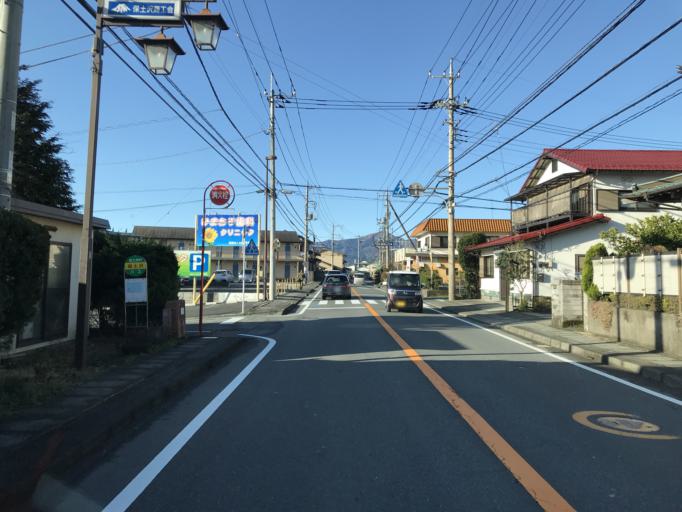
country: JP
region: Shizuoka
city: Gotemba
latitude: 35.2964
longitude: 138.9025
